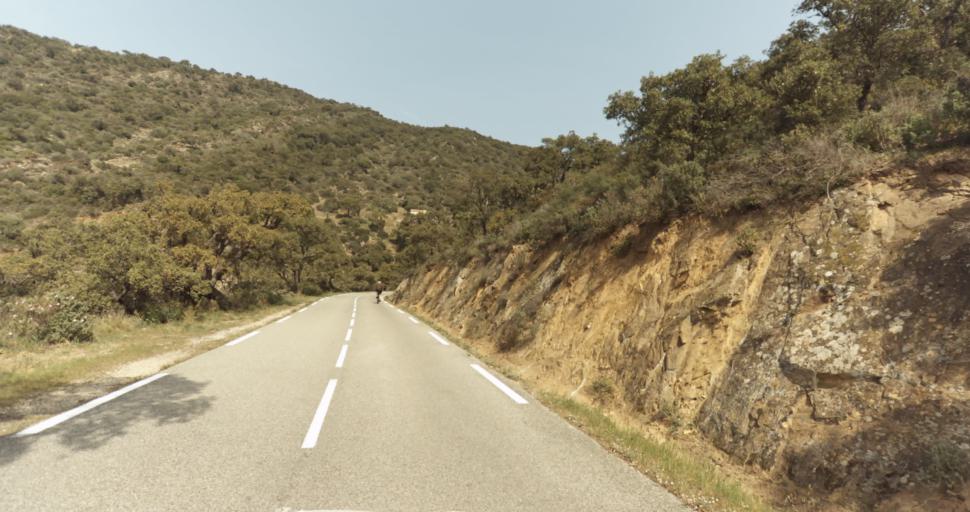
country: FR
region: Provence-Alpes-Cote d'Azur
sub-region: Departement du Var
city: Bormes-les-Mimosas
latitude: 43.1623
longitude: 6.3436
